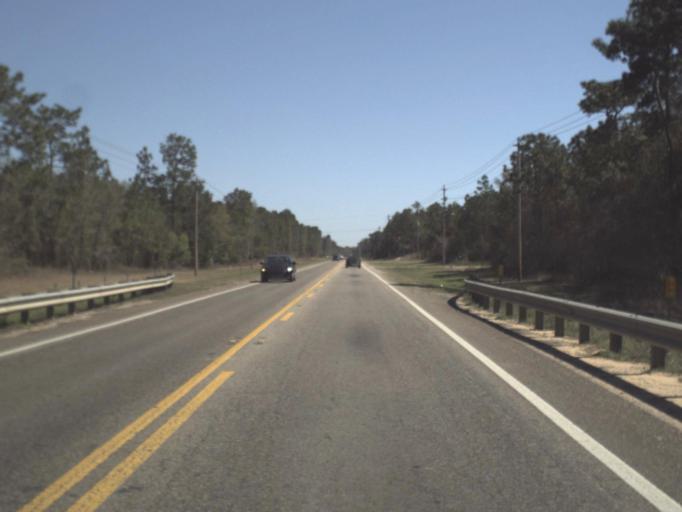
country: US
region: Florida
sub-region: Leon County
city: Tallahassee
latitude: 30.3873
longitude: -84.3129
